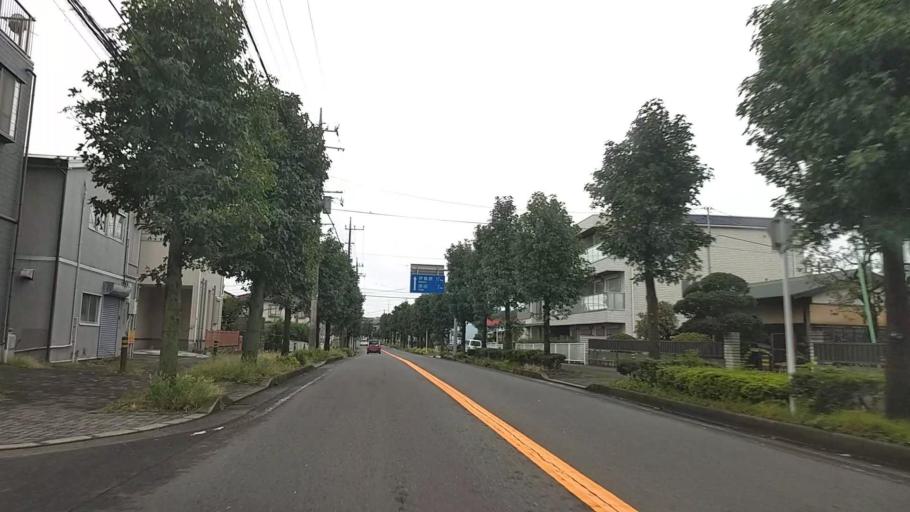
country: JP
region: Kanagawa
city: Fujisawa
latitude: 35.4146
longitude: 139.4750
